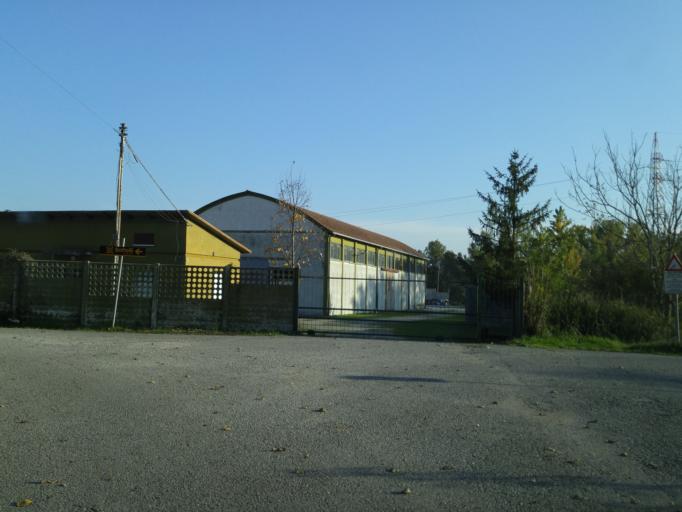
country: IT
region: The Marches
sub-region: Provincia di Pesaro e Urbino
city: Montefelcino
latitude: 43.7124
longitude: 12.8519
